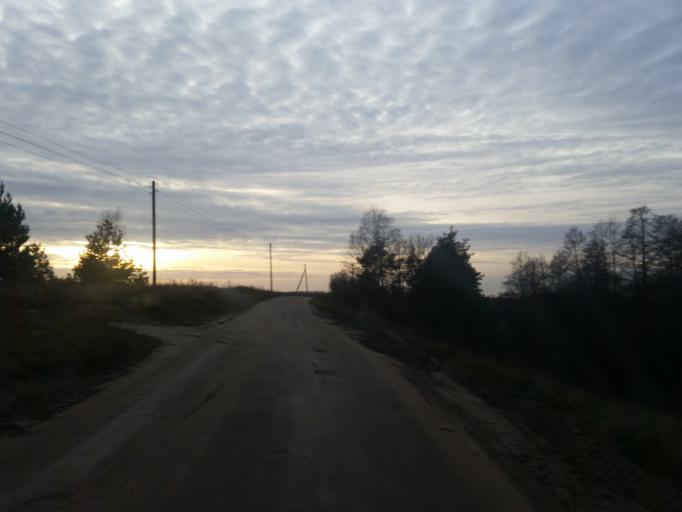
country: PL
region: Kujawsko-Pomorskie
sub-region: Powiat brodnicki
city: Brodnica
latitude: 53.2203
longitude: 19.3411
